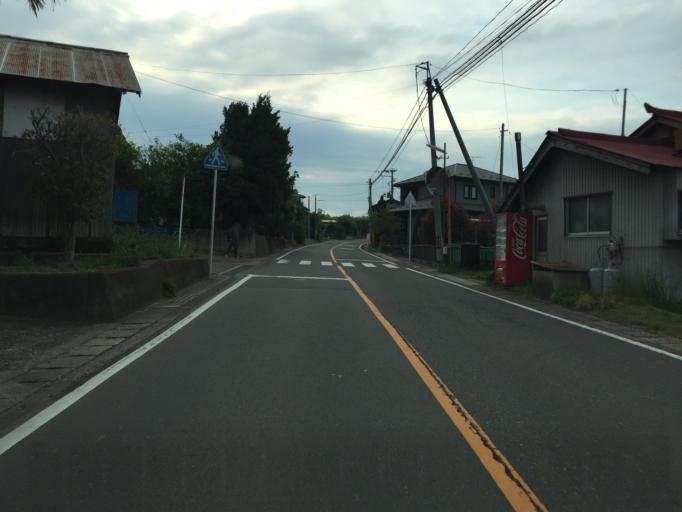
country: JP
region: Fukushima
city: Yanagawamachi-saiwaicho
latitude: 37.8752
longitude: 140.6014
